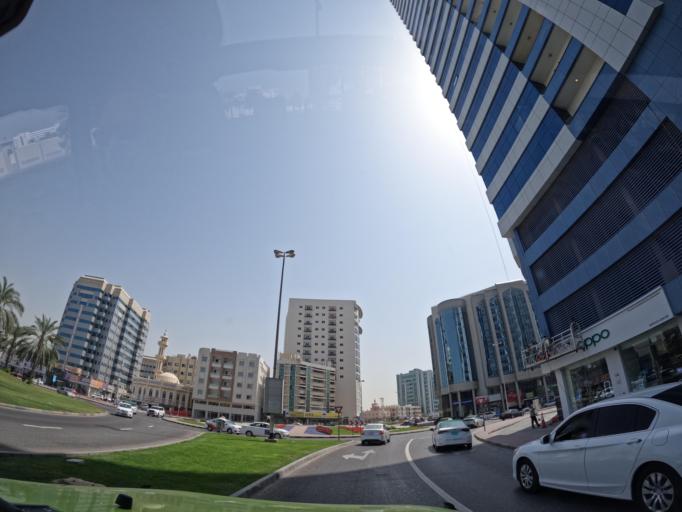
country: AE
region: Ajman
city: Ajman
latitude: 25.4165
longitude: 55.4426
